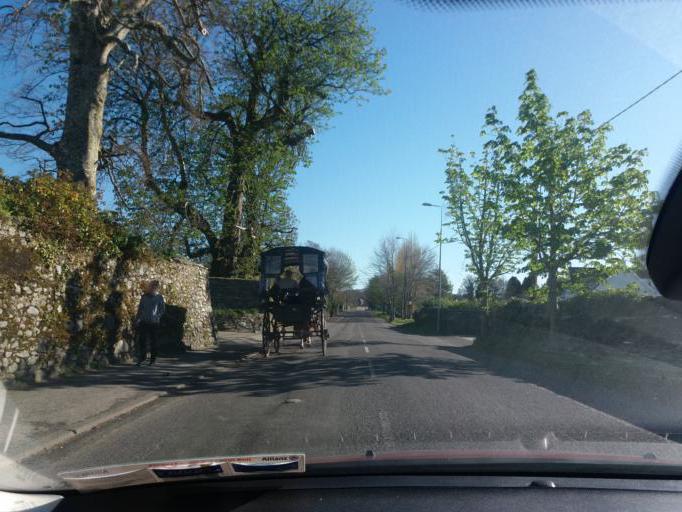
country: IE
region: Munster
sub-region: Ciarrai
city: Cill Airne
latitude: 52.0520
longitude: -9.5154
